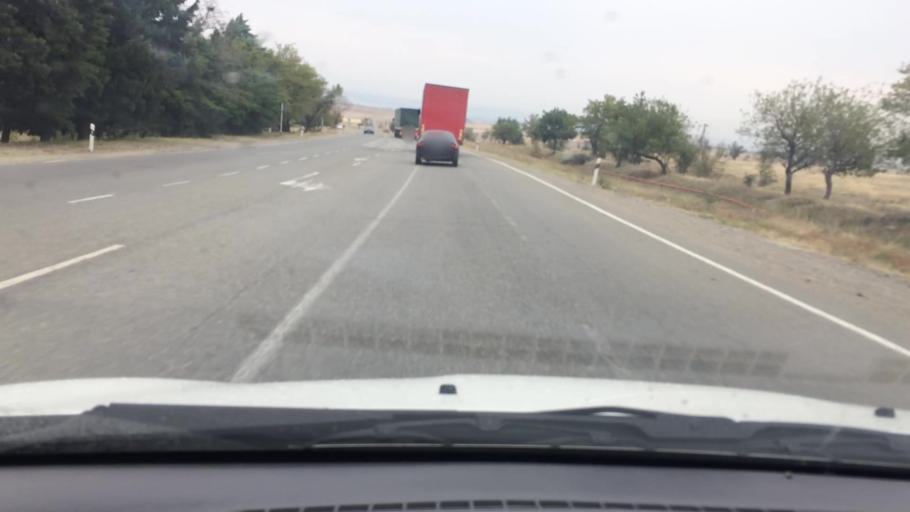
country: GE
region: T'bilisi
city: Tbilisi
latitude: 41.6392
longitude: 44.8693
